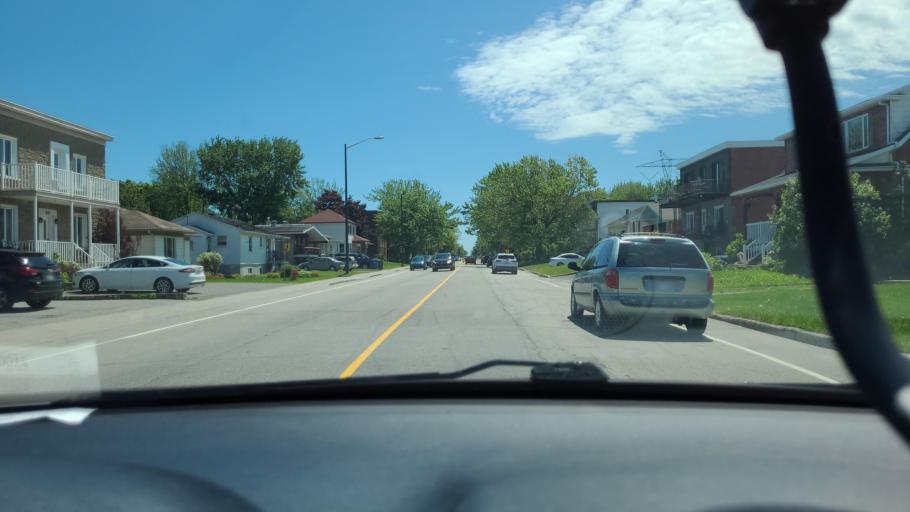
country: CA
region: Quebec
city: L'Ancienne-Lorette
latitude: 46.7650
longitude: -71.3270
